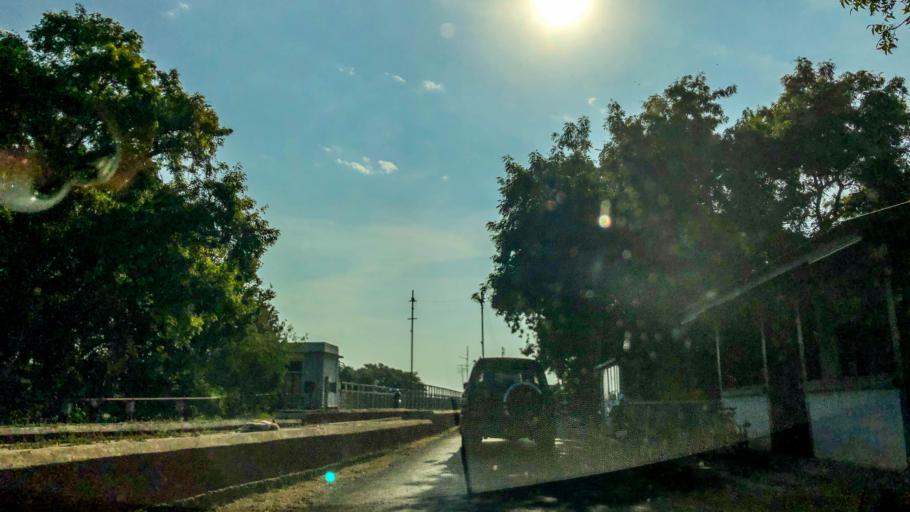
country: MM
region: Sagain
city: Sagaing
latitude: 21.8757
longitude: 95.9871
